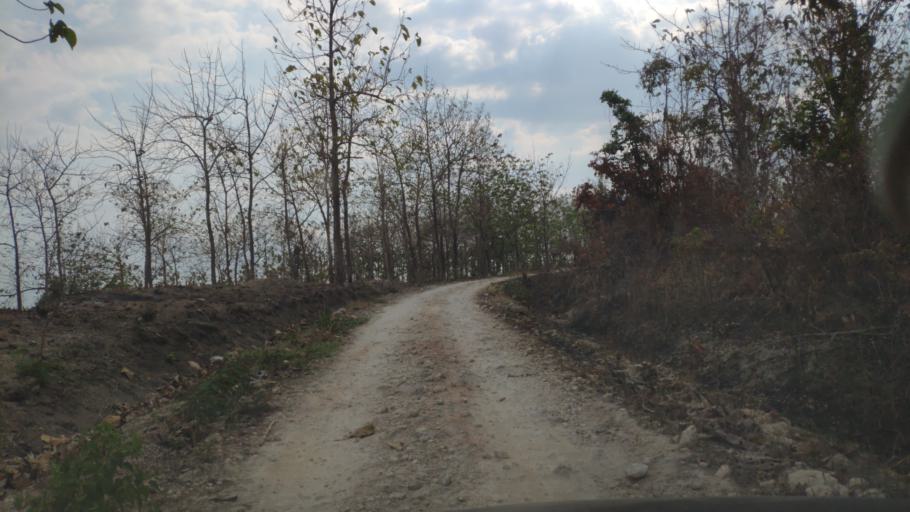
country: ID
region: Central Java
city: Randublatung
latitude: -7.3028
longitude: 111.3405
